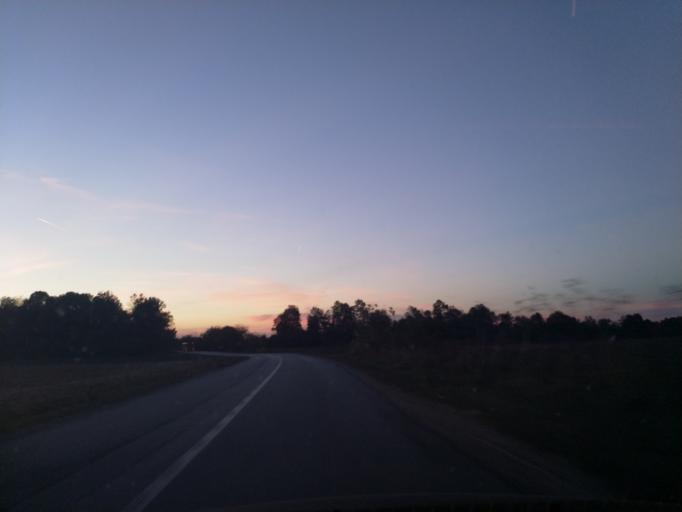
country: RS
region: Central Serbia
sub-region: Pomoravski Okrug
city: Svilajnac
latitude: 44.2370
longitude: 21.1355
